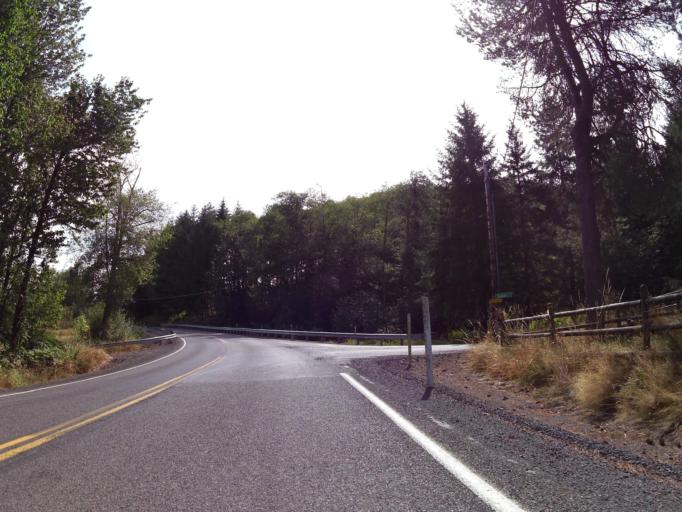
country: US
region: Washington
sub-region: Lewis County
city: Napavine
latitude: 46.5623
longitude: -122.9654
